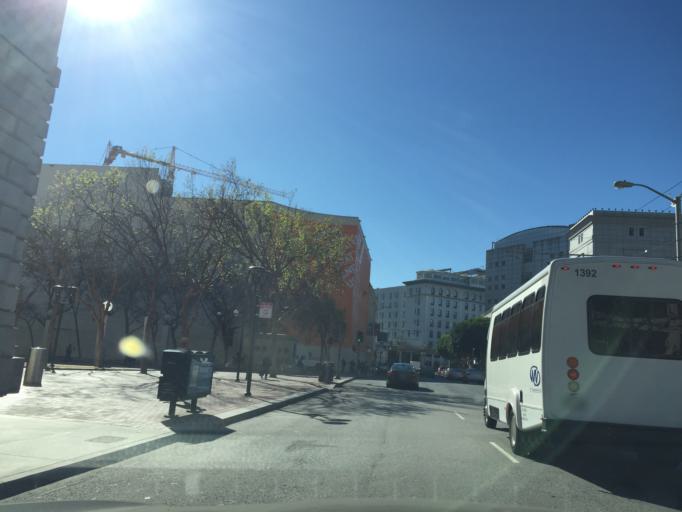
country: US
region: California
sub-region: San Francisco County
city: San Francisco
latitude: 37.7802
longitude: -122.4152
